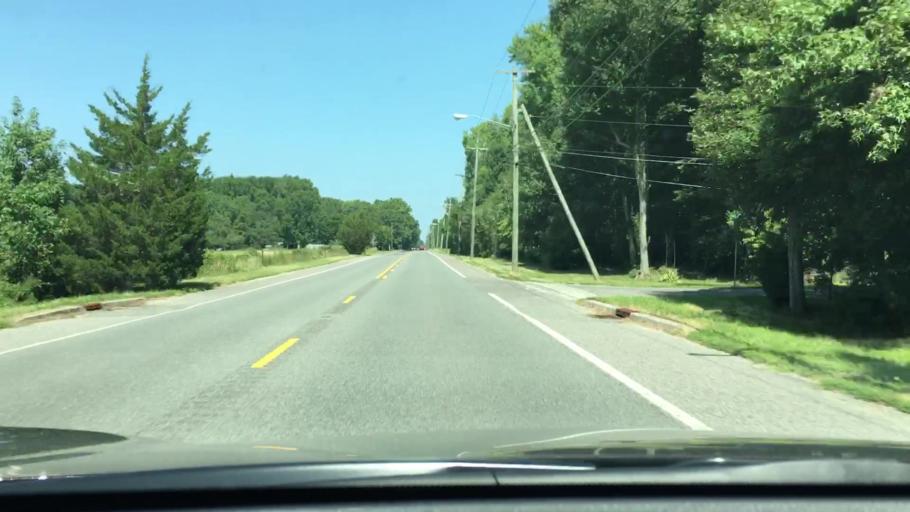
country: US
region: New Jersey
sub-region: Cumberland County
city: Laurel Lake
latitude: 39.3049
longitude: -75.0043
